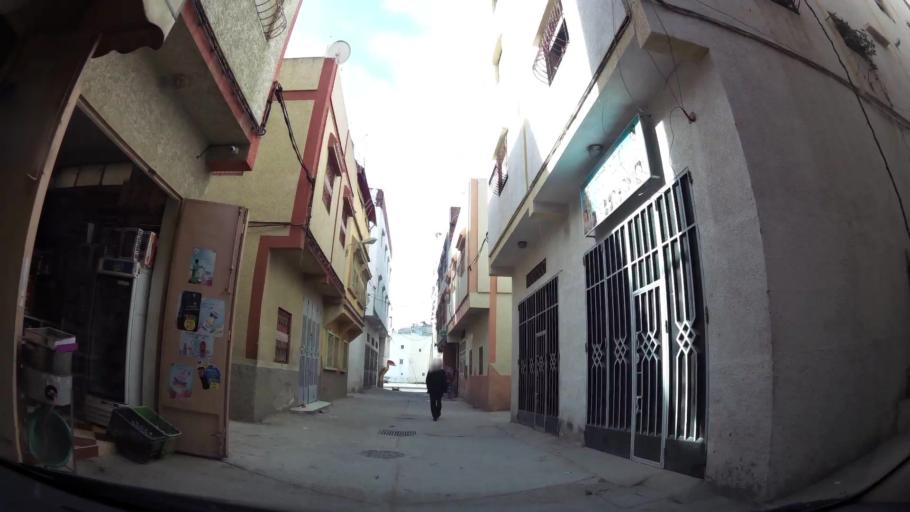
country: MA
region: Tanger-Tetouan
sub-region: Tanger-Assilah
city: Tangier
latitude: 35.7585
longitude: -5.7888
